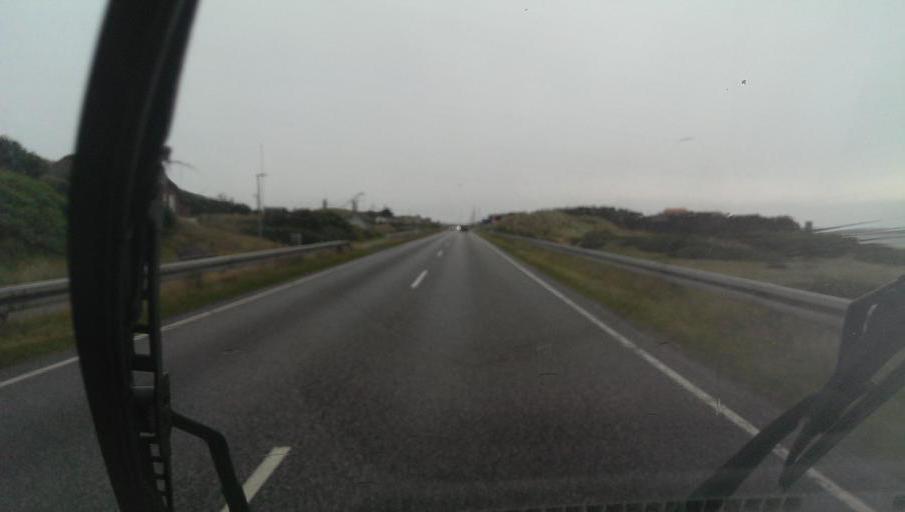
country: DK
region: Central Jutland
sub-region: Ringkobing-Skjern Kommune
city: Hvide Sande
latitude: 55.9899
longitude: 8.1334
